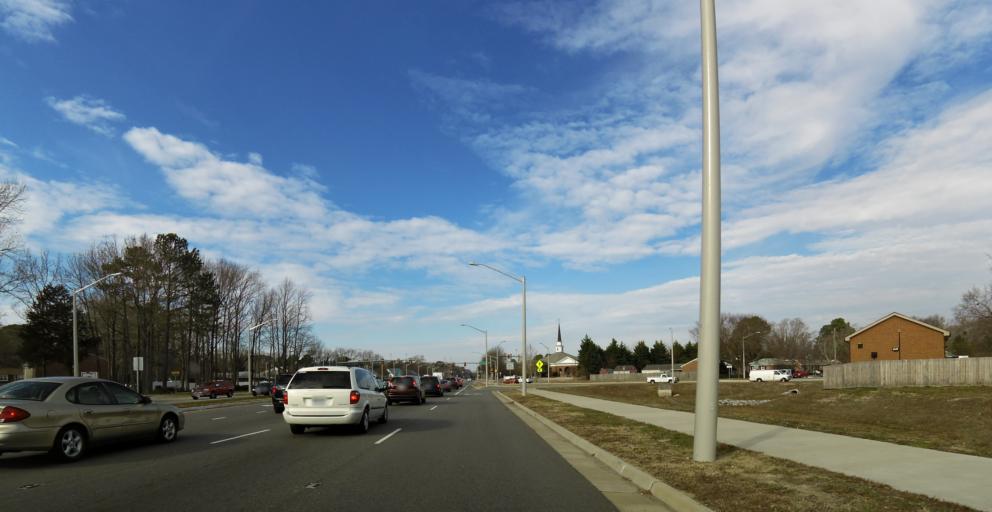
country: US
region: Virginia
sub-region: City of Newport News
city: Newport News
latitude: 37.0865
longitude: -76.4994
